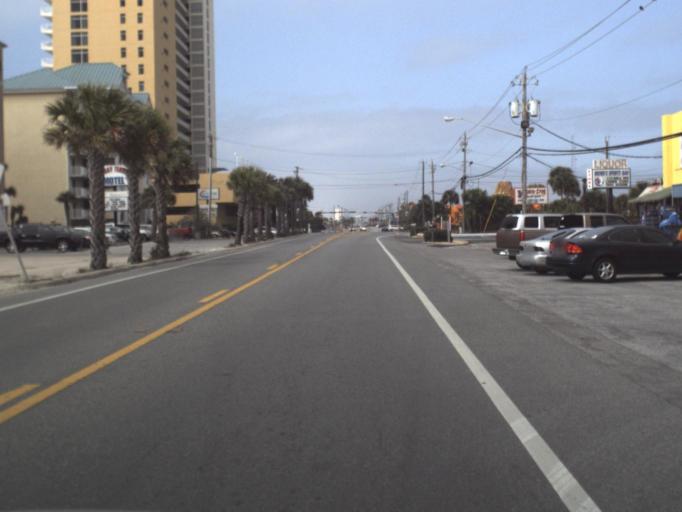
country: US
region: Florida
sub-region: Bay County
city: Panama City Beach
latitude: 30.1879
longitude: -85.8260
